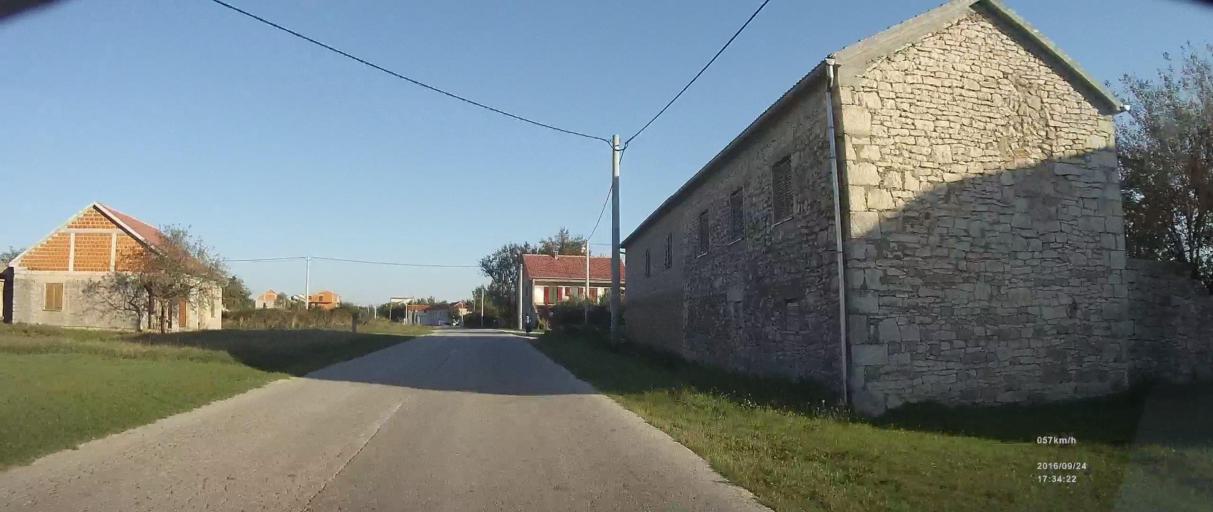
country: HR
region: Zadarska
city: Posedarje
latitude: 44.1675
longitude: 15.4590
